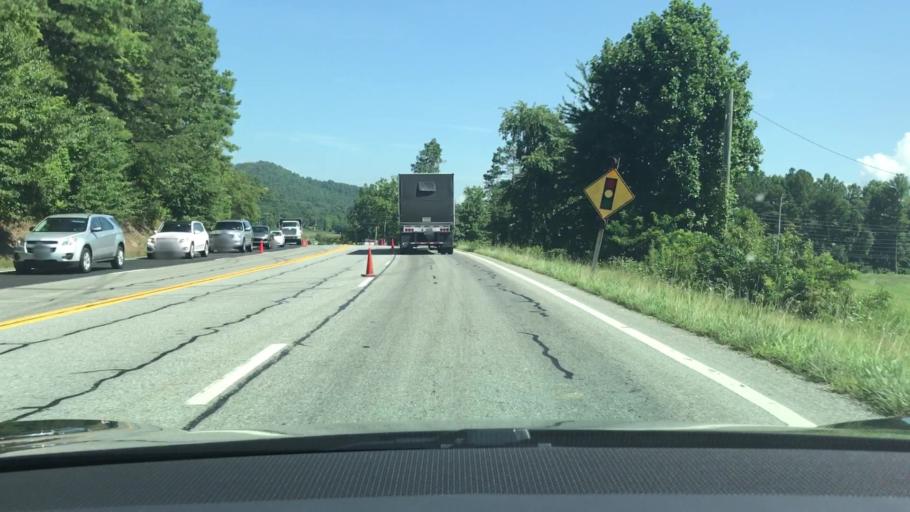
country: US
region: Georgia
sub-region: Rabun County
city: Mountain City
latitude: 34.9553
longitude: -83.3861
